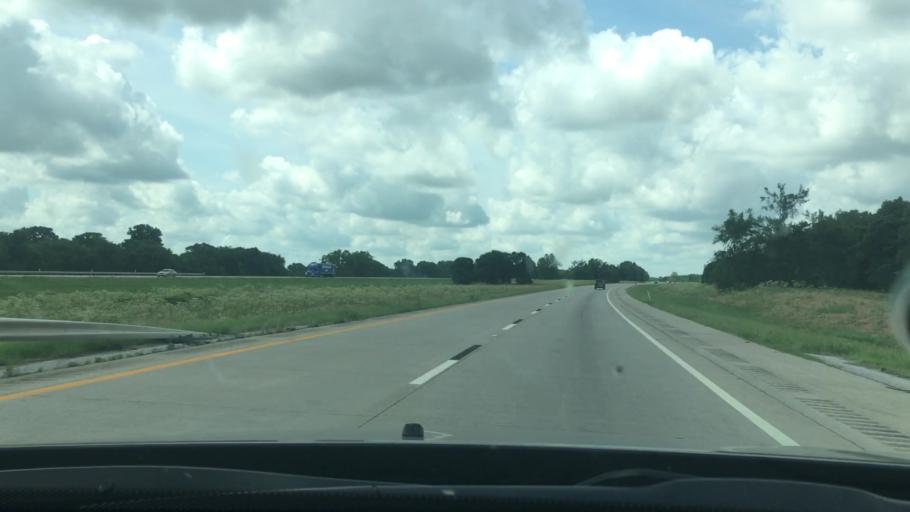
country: US
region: Oklahoma
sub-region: Love County
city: Marietta
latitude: 33.8220
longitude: -97.1309
